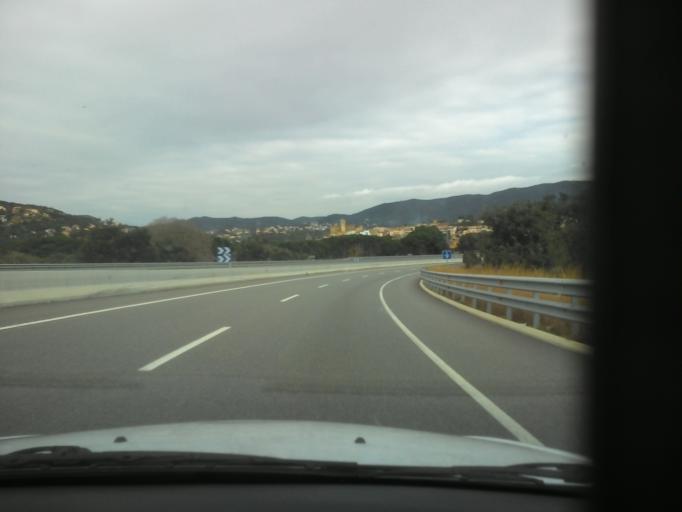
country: ES
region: Catalonia
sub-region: Provincia de Girona
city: Calonge
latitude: 41.8547
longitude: 3.0726
